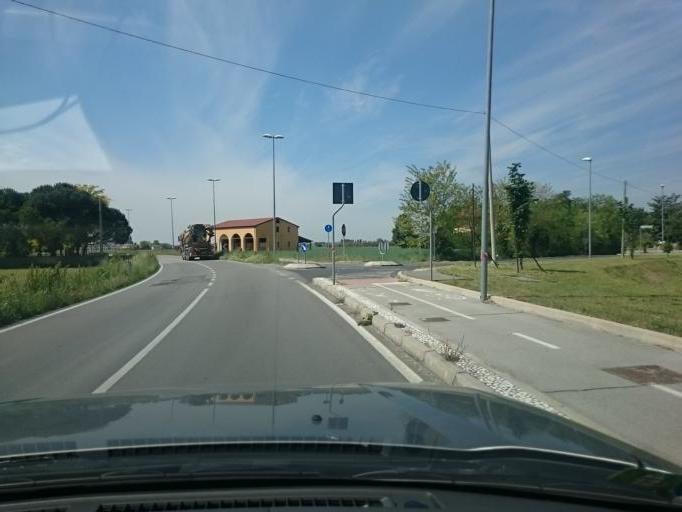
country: IT
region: Veneto
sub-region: Provincia di Padova
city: Monselice
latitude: 45.2215
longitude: 11.7391
